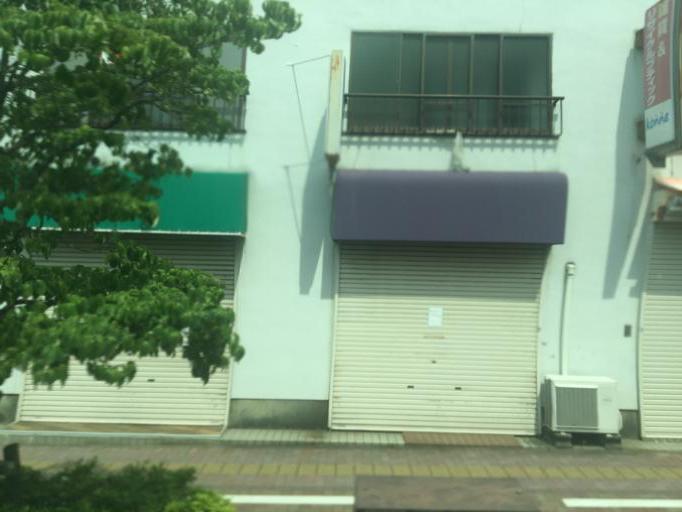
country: JP
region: Tokyo
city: Tanashicho
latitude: 35.7551
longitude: 139.5478
